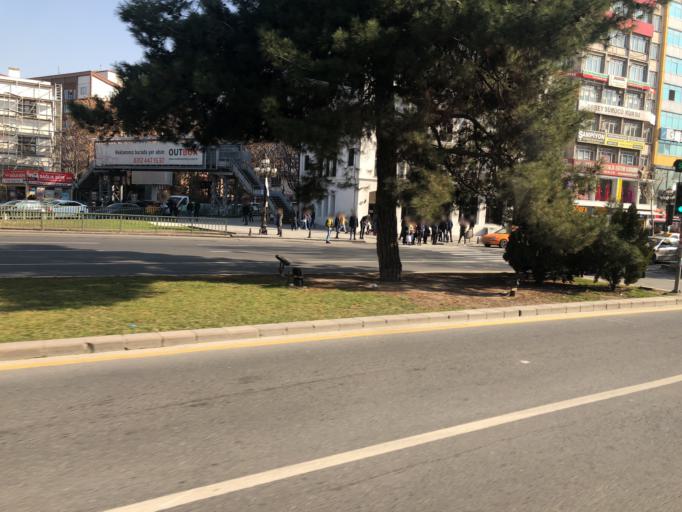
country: TR
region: Ankara
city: Ankara
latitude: 39.9266
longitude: 32.8549
